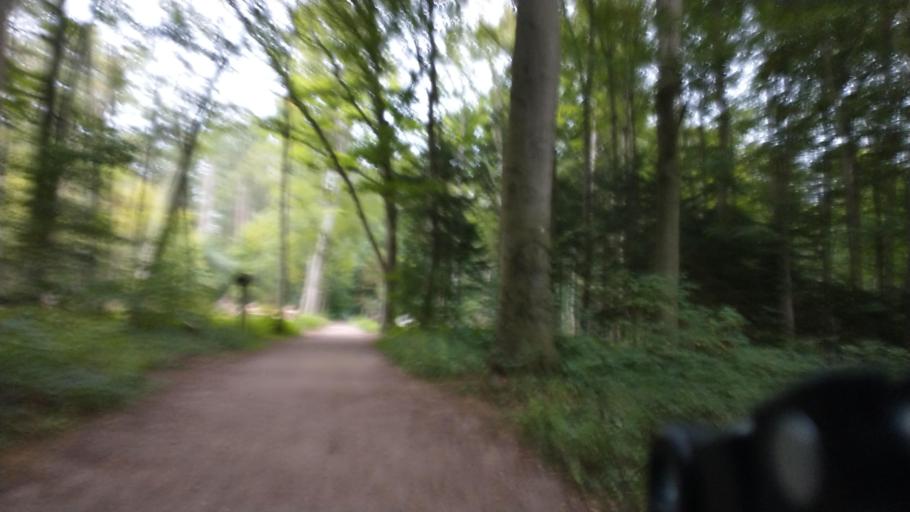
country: DE
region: Schleswig-Holstein
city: Grabau
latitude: 53.7973
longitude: 10.2619
